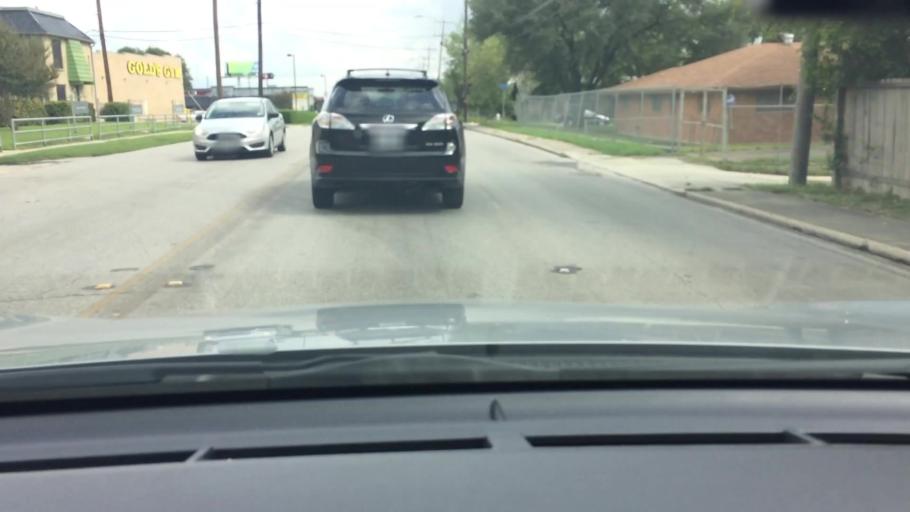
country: US
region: Texas
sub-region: Bexar County
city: Castle Hills
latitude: 29.5436
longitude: -98.5312
